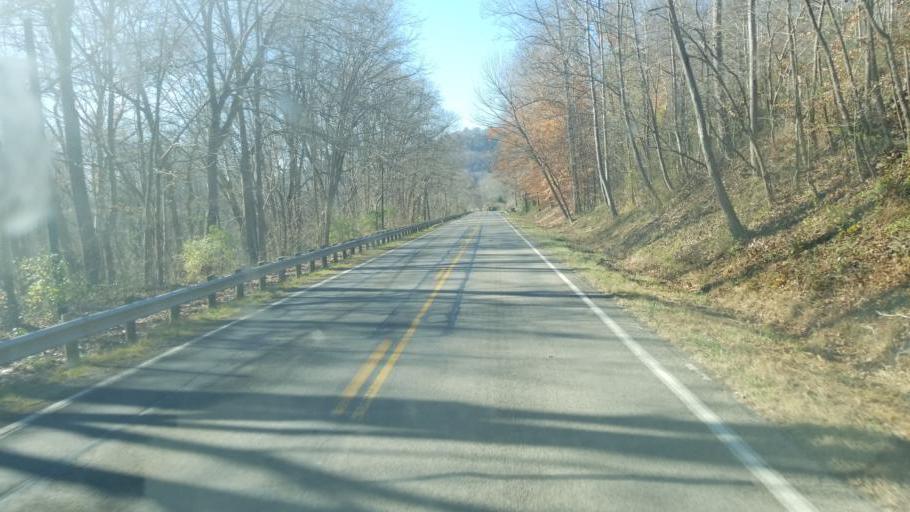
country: US
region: Kentucky
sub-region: Lewis County
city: Vanceburg
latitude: 38.6353
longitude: -83.2456
